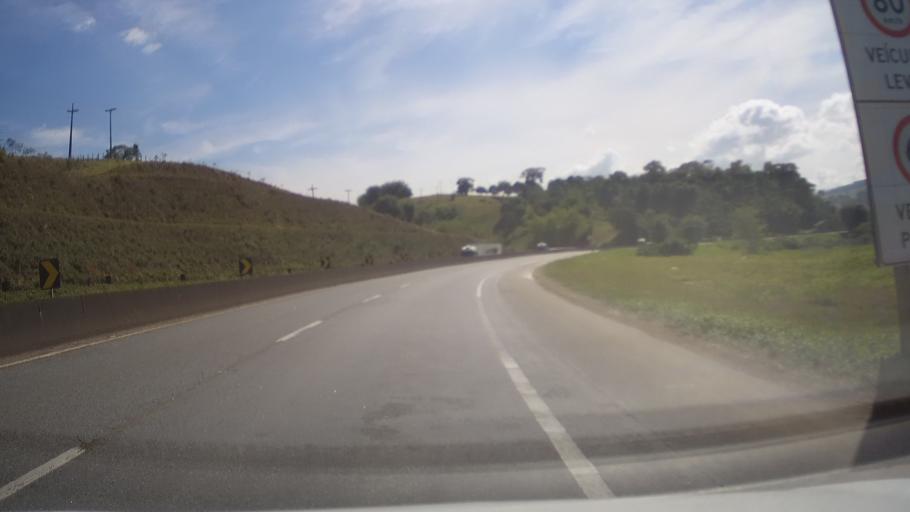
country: BR
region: Minas Gerais
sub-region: Cambui
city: Cambui
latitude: -22.5341
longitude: -46.0342
